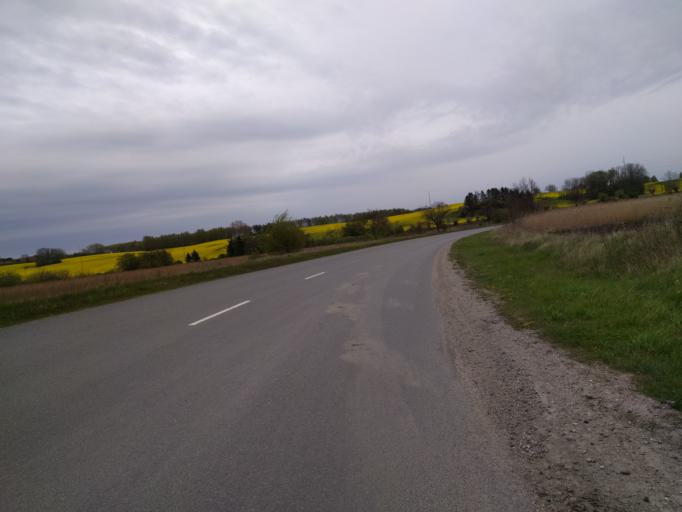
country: DK
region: South Denmark
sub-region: Kerteminde Kommune
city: Munkebo
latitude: 55.4709
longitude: 10.5520
